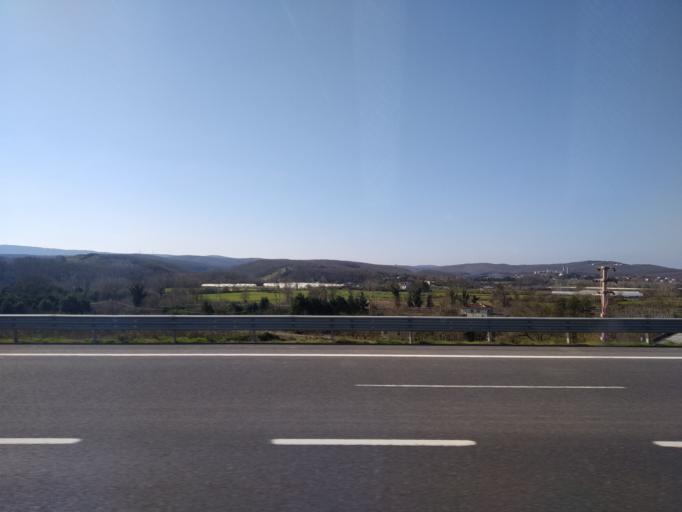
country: TR
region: Istanbul
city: Mahmut Sevket Pasa
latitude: 41.1238
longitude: 29.2864
